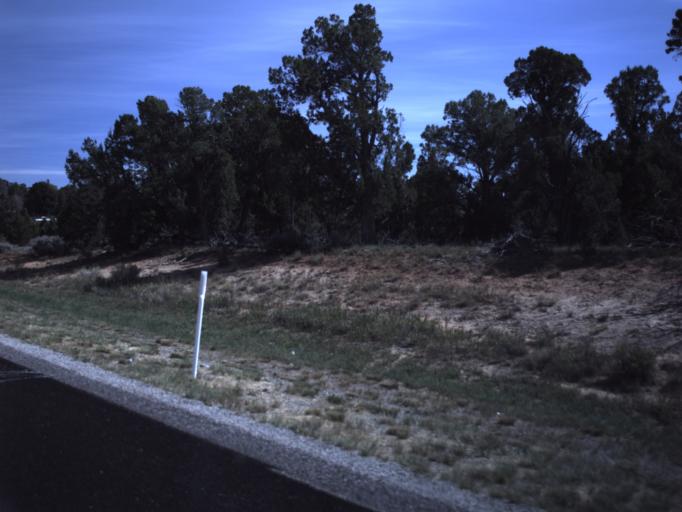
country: US
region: Utah
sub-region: San Juan County
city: Monticello
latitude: 37.8585
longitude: -109.2010
